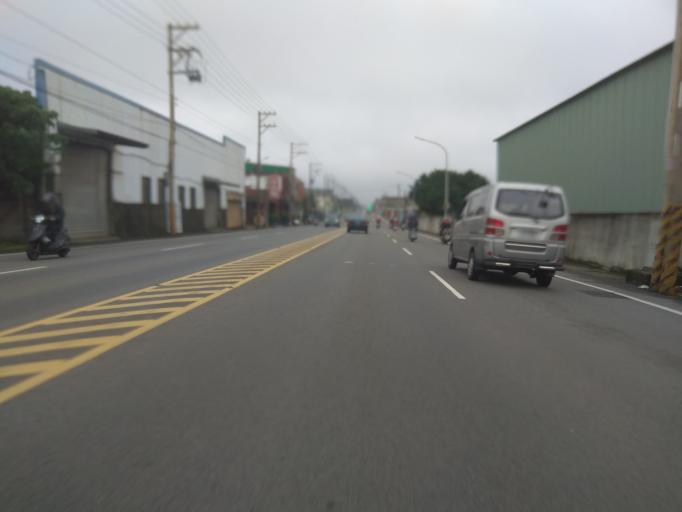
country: TW
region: Taiwan
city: Taoyuan City
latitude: 25.0228
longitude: 121.1169
